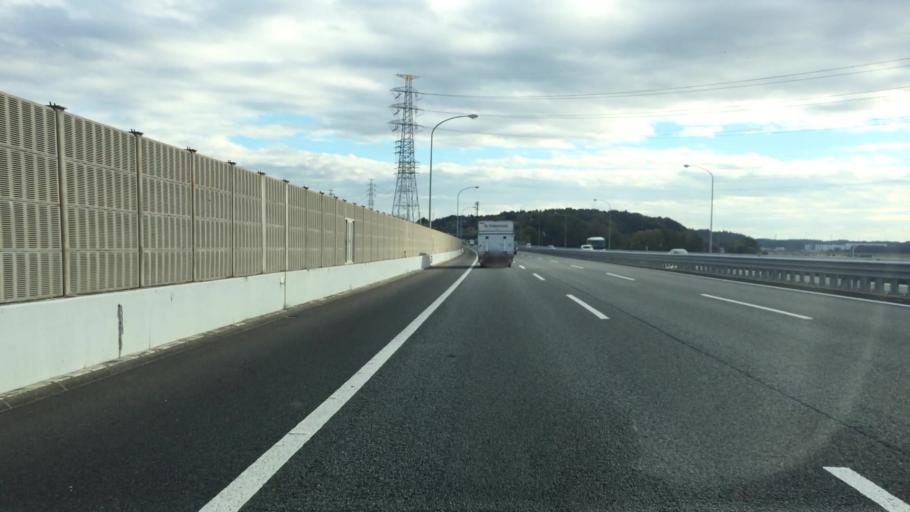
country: JP
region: Chiba
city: Yotsukaido
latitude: 35.6823
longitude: 140.2003
